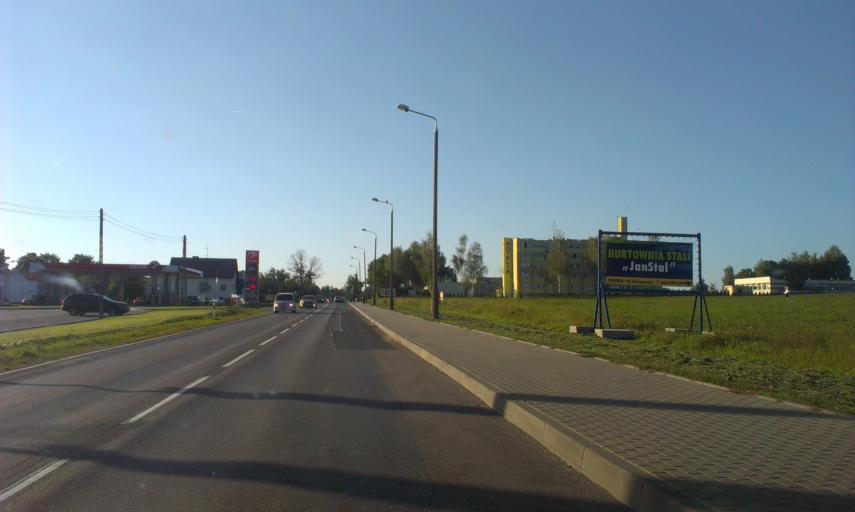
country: PL
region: Kujawsko-Pomorskie
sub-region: Powiat tucholski
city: Tuchola
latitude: 53.5787
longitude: 17.8769
